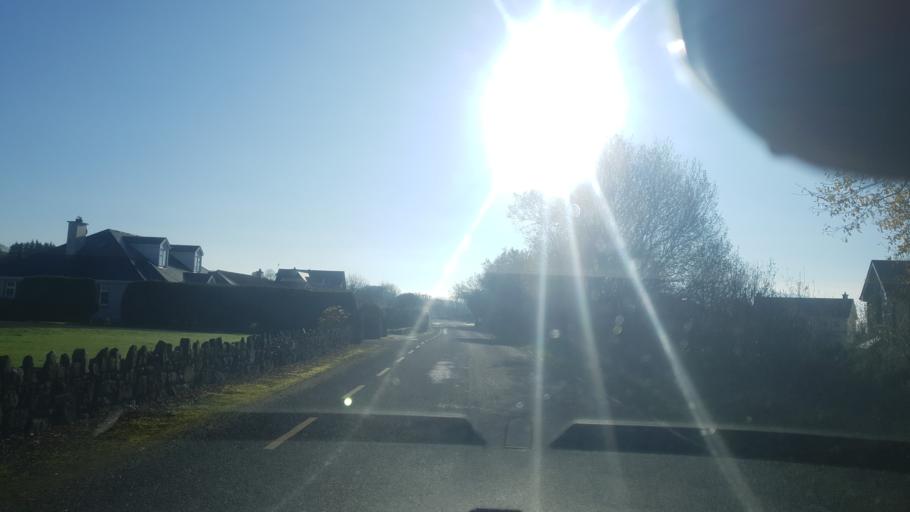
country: IE
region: Munster
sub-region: Ciarrai
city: Cill Airne
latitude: 52.1012
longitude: -9.4720
